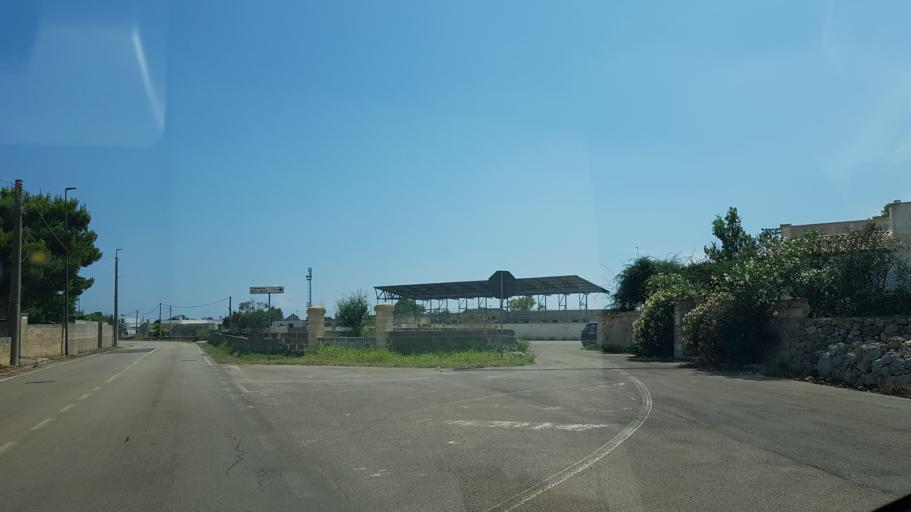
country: IT
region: Apulia
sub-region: Provincia di Lecce
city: Castrignano del Capo
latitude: 39.8263
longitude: 18.3522
